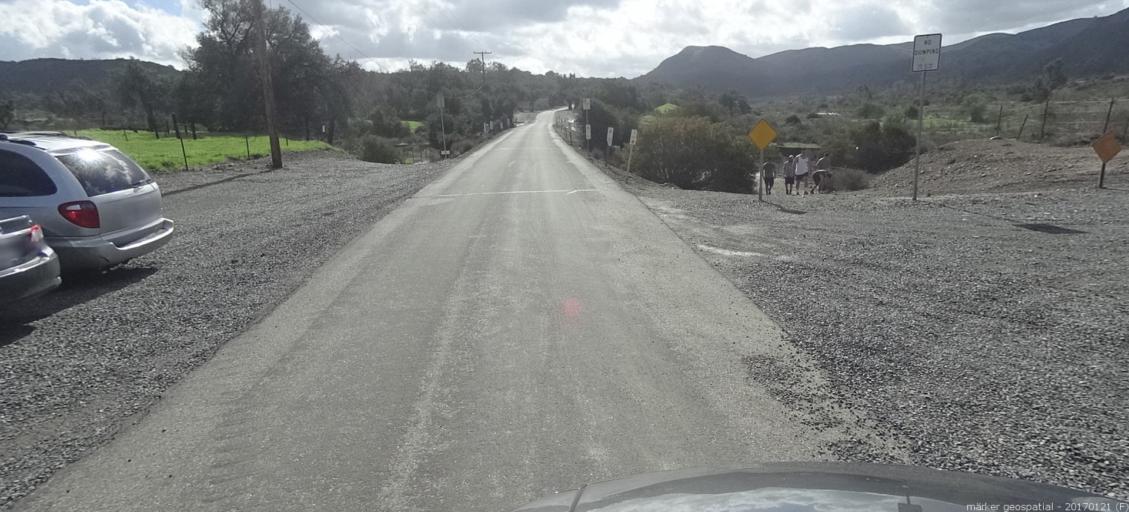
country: US
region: California
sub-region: Orange County
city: Foothill Ranch
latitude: 33.7629
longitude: -117.6776
